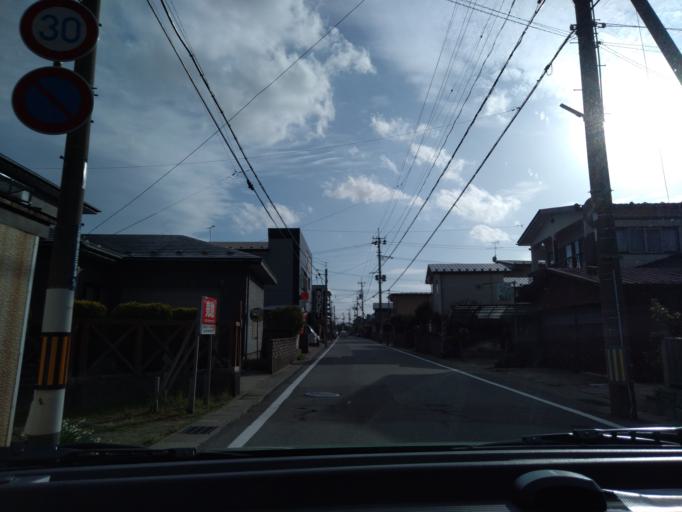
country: JP
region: Akita
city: Akita Shi
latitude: 39.7687
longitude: 140.0826
